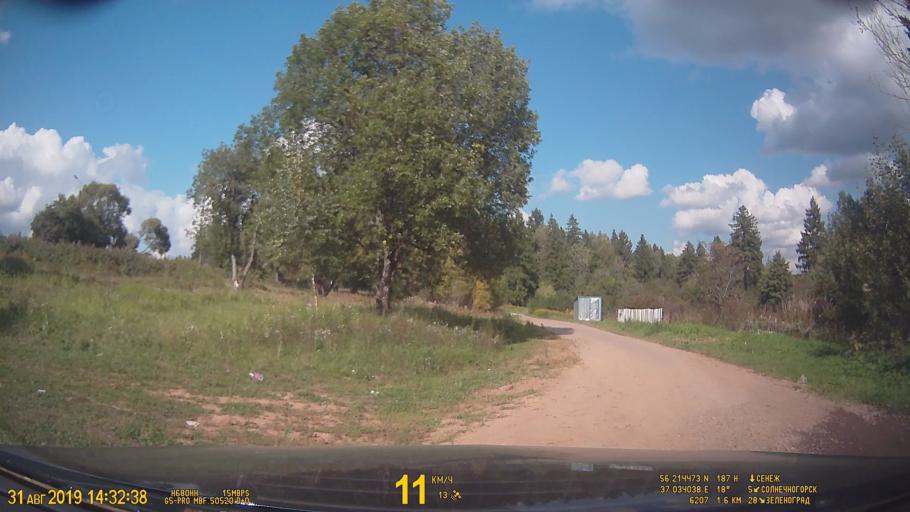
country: RU
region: Moskovskaya
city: Solnechnogorsk
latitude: 56.2145
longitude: 37.0341
